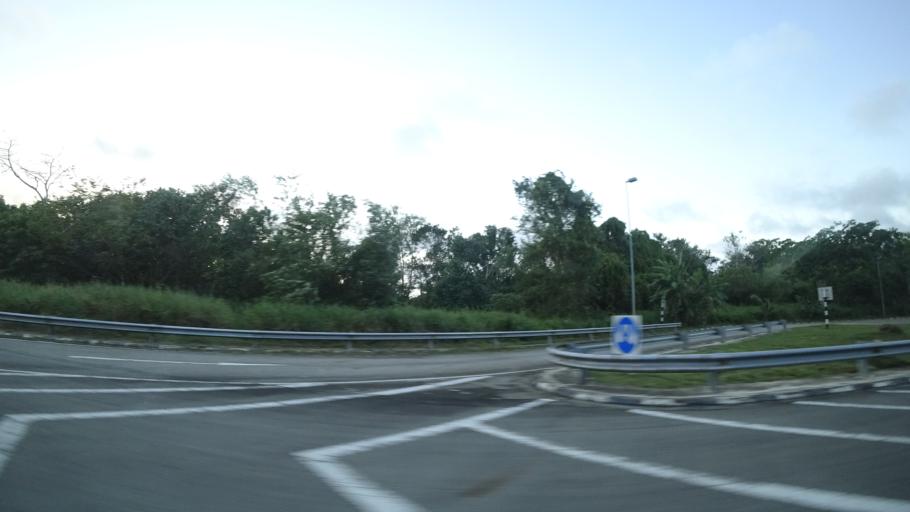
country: BN
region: Tutong
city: Tutong
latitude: 4.8730
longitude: 114.7891
